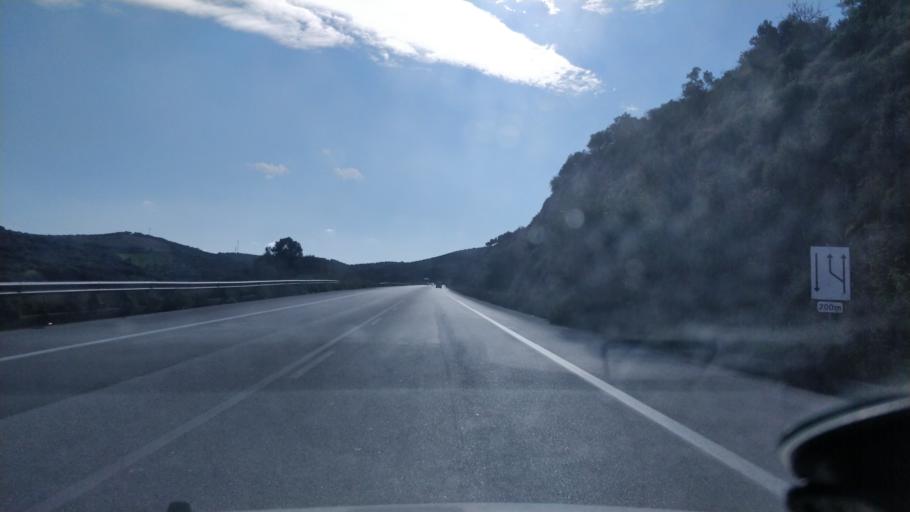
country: GR
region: Crete
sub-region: Nomos Irakleiou
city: Ano Arhanes
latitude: 35.2556
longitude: 25.1791
